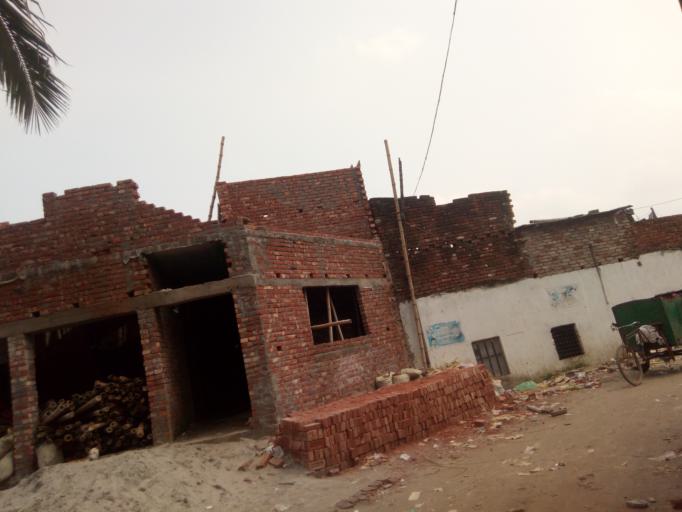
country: BD
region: Dhaka
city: Azimpur
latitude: 23.7428
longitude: 90.3587
